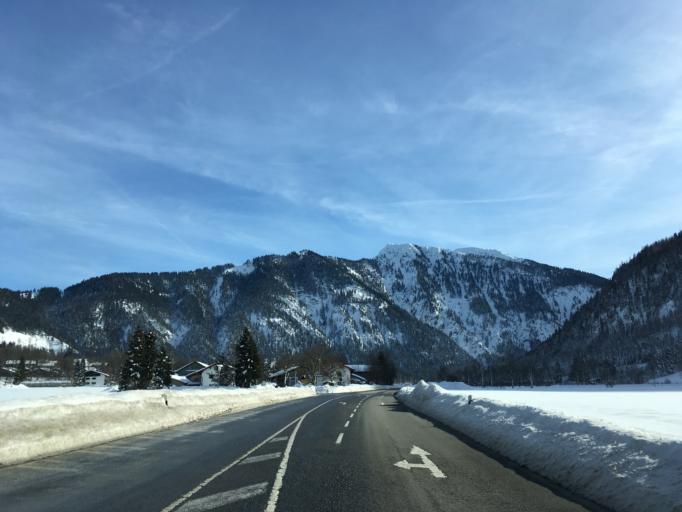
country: DE
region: Bavaria
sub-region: Upper Bavaria
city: Bayrischzell
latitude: 47.6791
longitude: 12.0023
